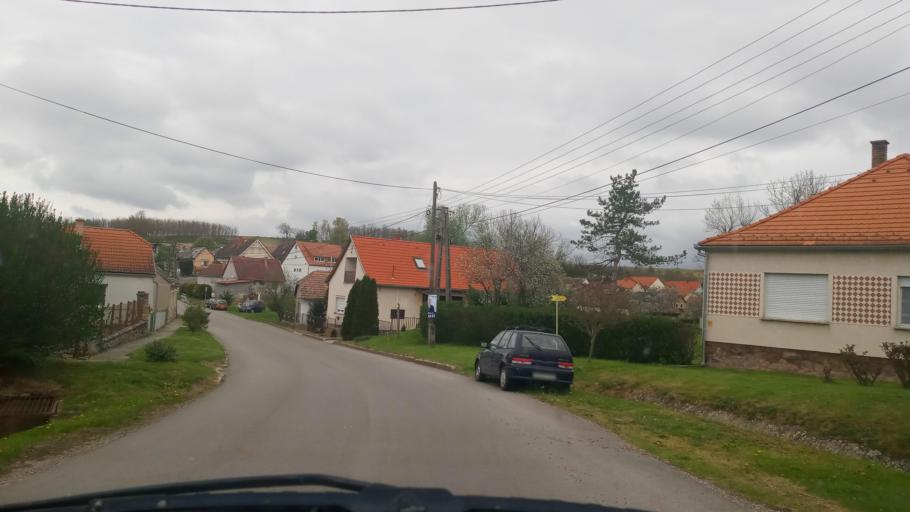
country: HU
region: Baranya
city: Kozarmisleny
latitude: 46.0402
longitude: 18.3489
